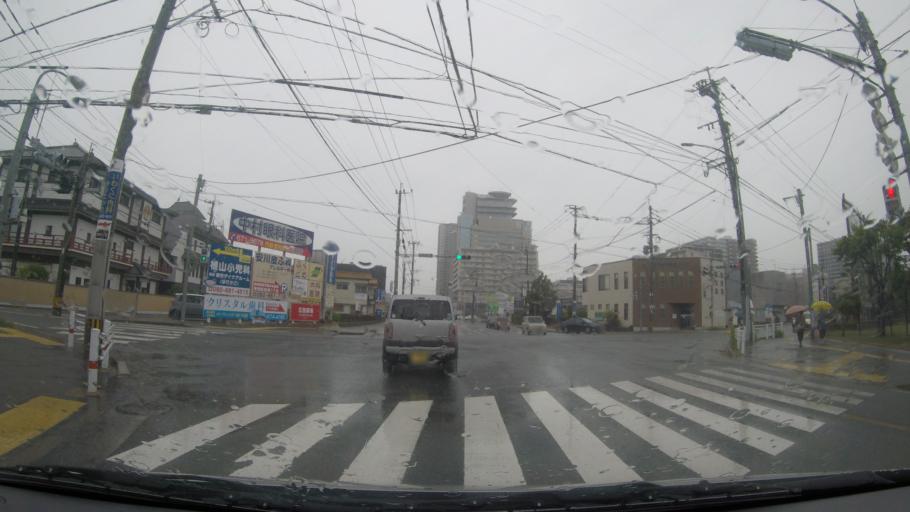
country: JP
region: Fukuoka
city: Fukuoka-shi
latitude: 33.6464
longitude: 130.4419
